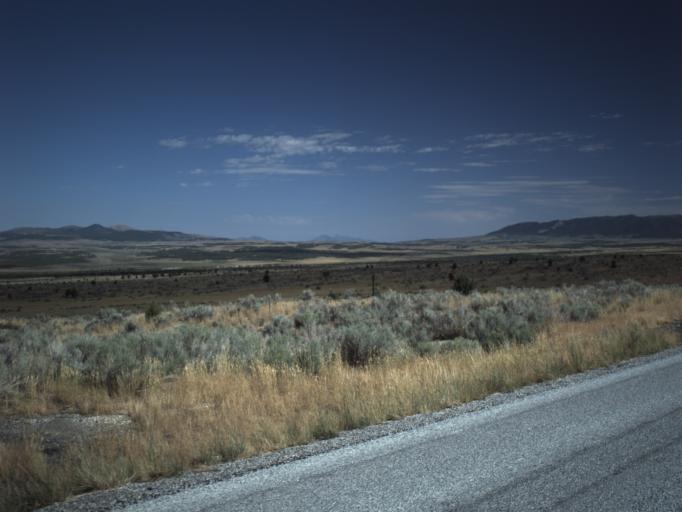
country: US
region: Utah
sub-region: Juab County
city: Mona
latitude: 39.8016
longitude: -112.1450
